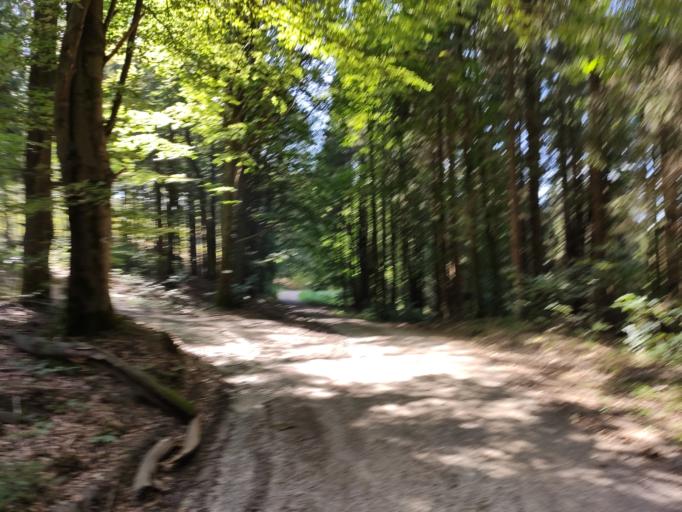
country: DE
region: Bavaria
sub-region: Upper Franconia
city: Nordhalben
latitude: 50.4143
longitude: 11.5374
